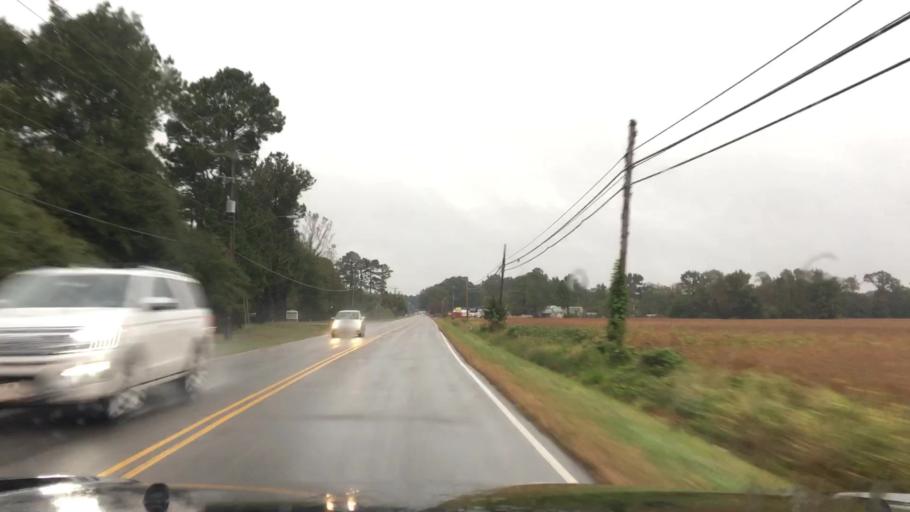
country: US
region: North Carolina
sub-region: Currituck County
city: Moyock
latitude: 36.6678
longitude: -76.2269
